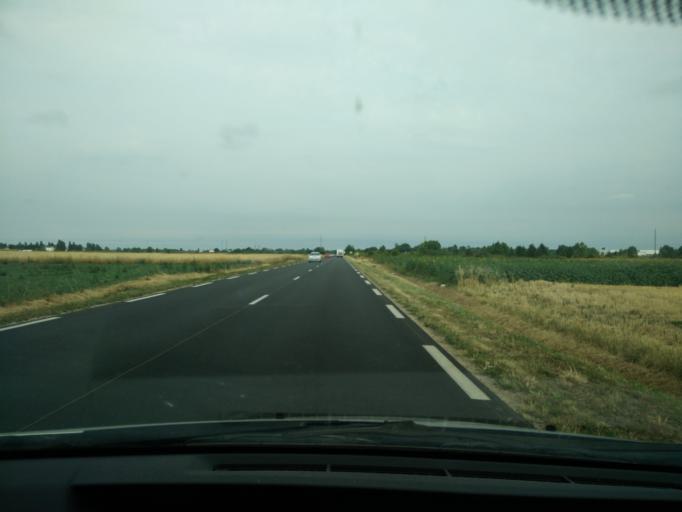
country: FR
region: Pays de la Loire
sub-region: Departement de Maine-et-Loire
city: Doue-la-Fontaine
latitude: 47.1775
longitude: -0.2353
